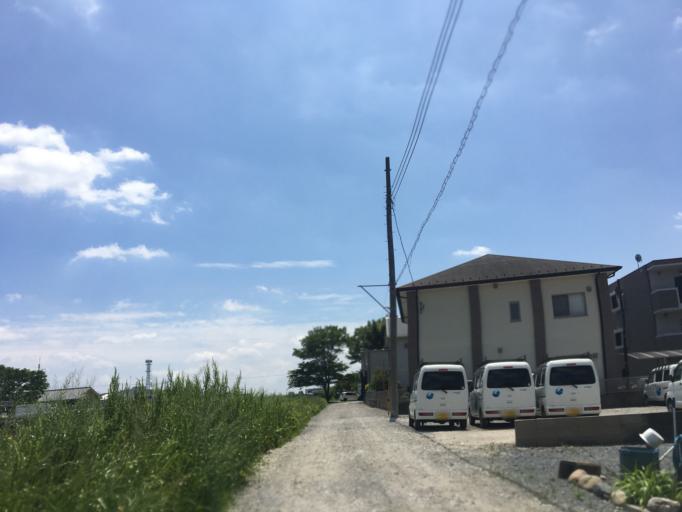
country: JP
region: Saitama
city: Shiki
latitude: 35.8637
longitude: 139.6014
